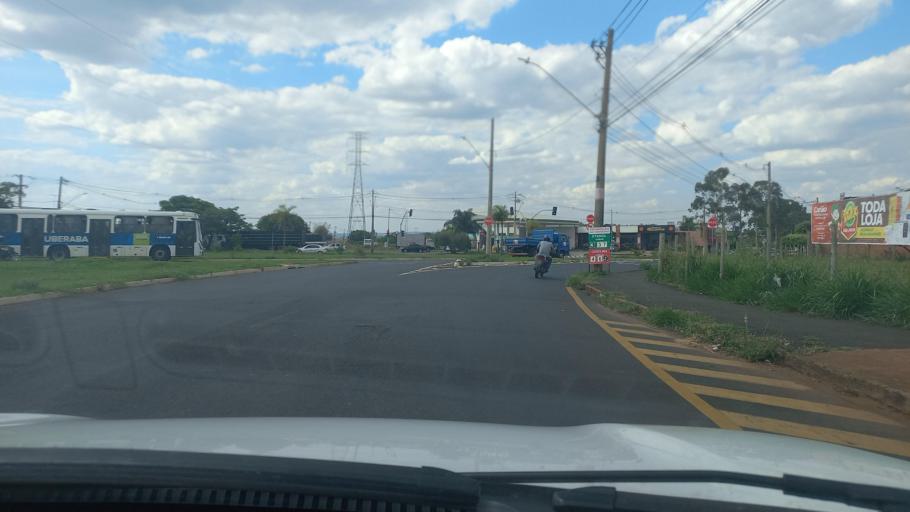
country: BR
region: Minas Gerais
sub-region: Uberaba
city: Uberaba
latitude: -19.7556
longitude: -47.9888
